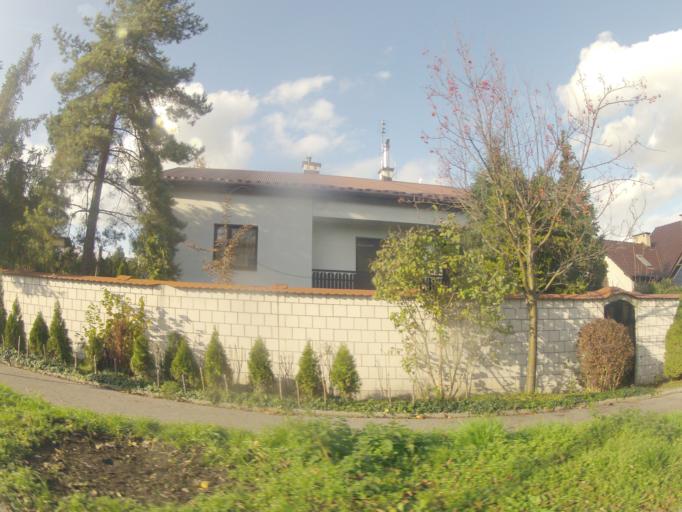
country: PL
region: Lesser Poland Voivodeship
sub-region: Powiat krakowski
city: Rzaska
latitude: 50.0684
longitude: 19.8536
